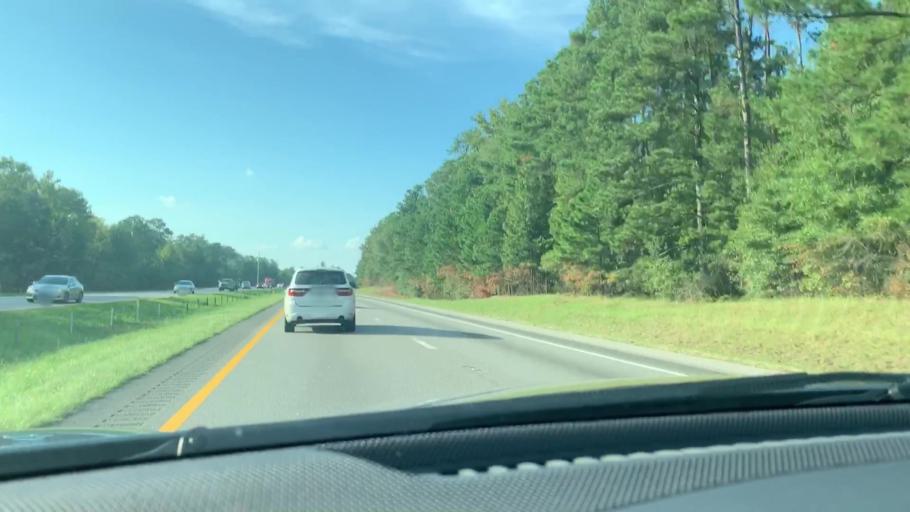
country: US
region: South Carolina
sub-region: Calhoun County
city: Oak Grove
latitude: 33.7788
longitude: -80.9836
